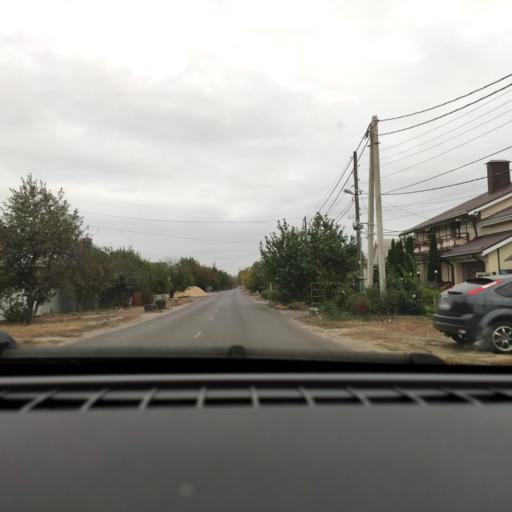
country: RU
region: Voronezj
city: Voronezh
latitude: 51.6665
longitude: 39.2578
